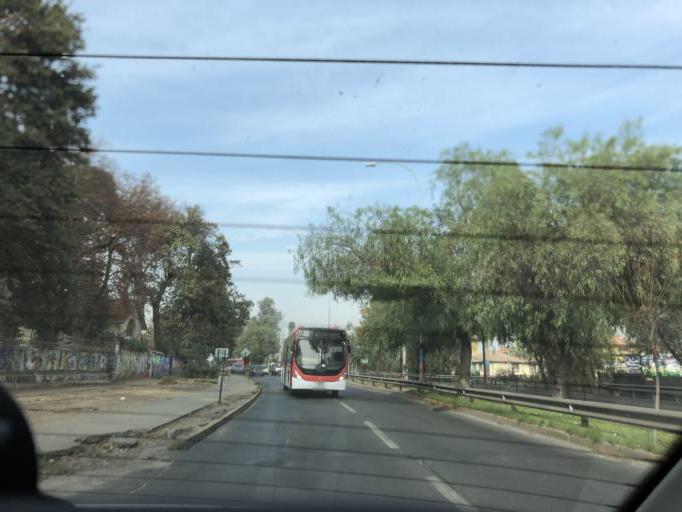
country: CL
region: Santiago Metropolitan
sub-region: Provincia de Cordillera
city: Puente Alto
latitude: -33.5647
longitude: -70.5551
